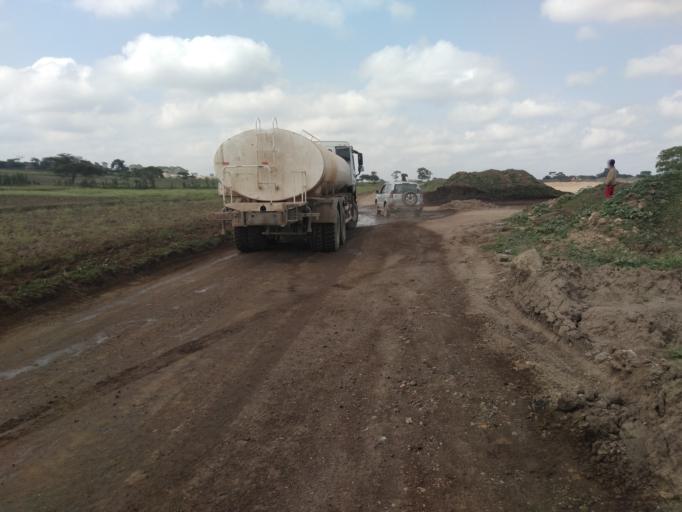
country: ET
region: Oromiya
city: Shashemene
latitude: 7.3999
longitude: 38.6600
